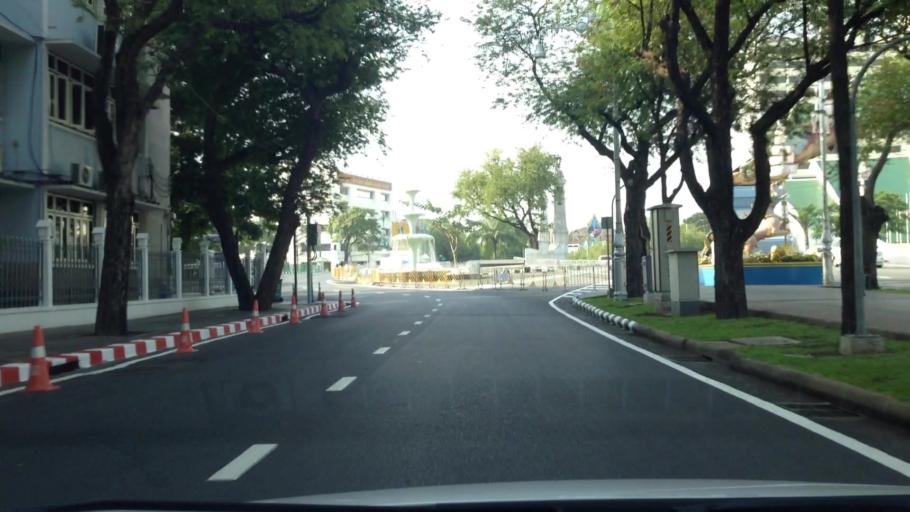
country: TH
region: Bangkok
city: Pom Prap Sattru Phai
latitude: 13.7644
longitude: 100.5100
